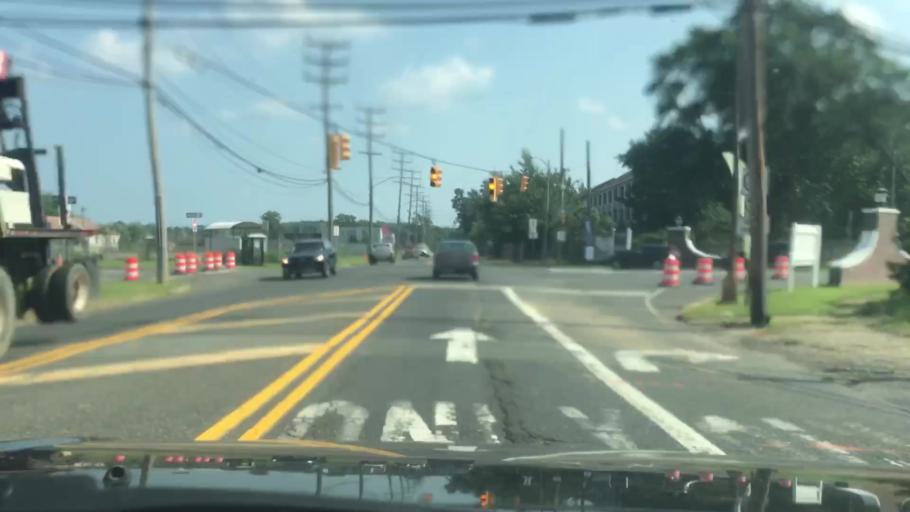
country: US
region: New Jersey
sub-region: Monmouth County
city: Oceanport
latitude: 40.3183
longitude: -74.0341
